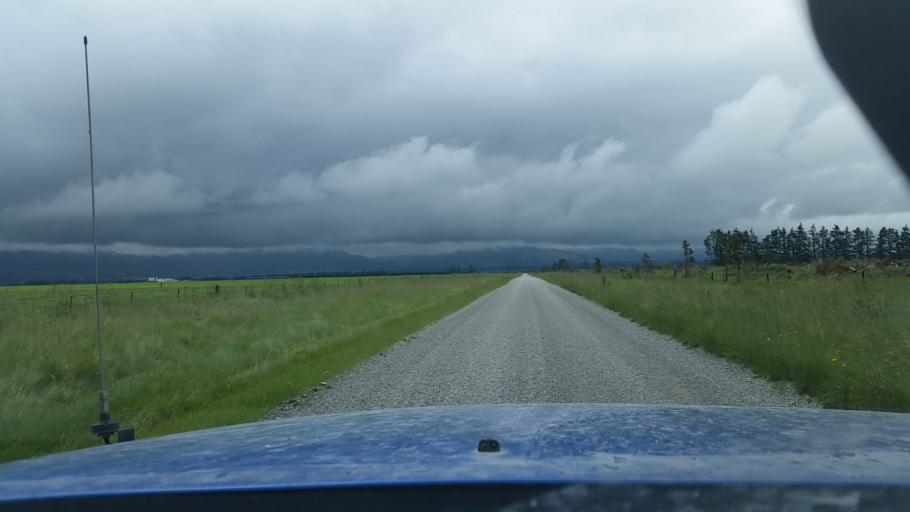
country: NZ
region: Canterbury
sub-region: Ashburton District
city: Methven
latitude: -43.7158
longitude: 171.4579
